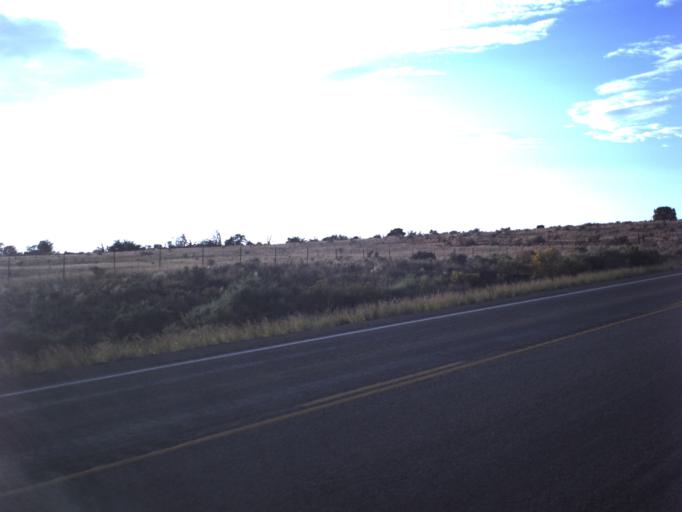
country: US
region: Utah
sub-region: San Juan County
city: Monticello
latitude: 38.2359
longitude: -109.3789
